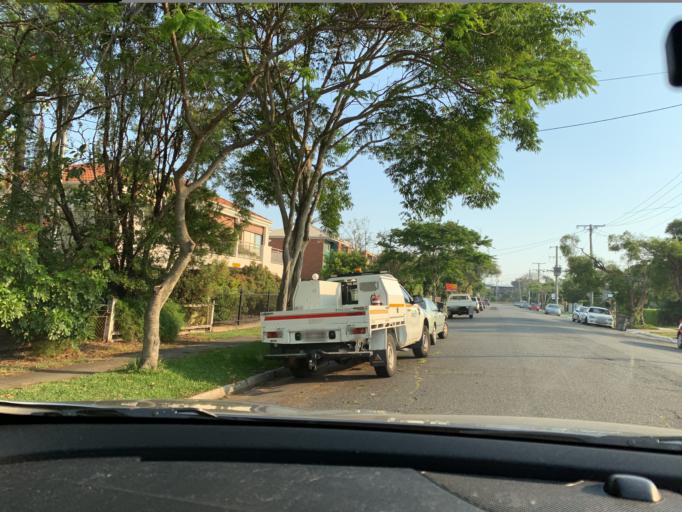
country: AU
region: Queensland
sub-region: Brisbane
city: Ascot
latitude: -27.4294
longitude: 153.0773
